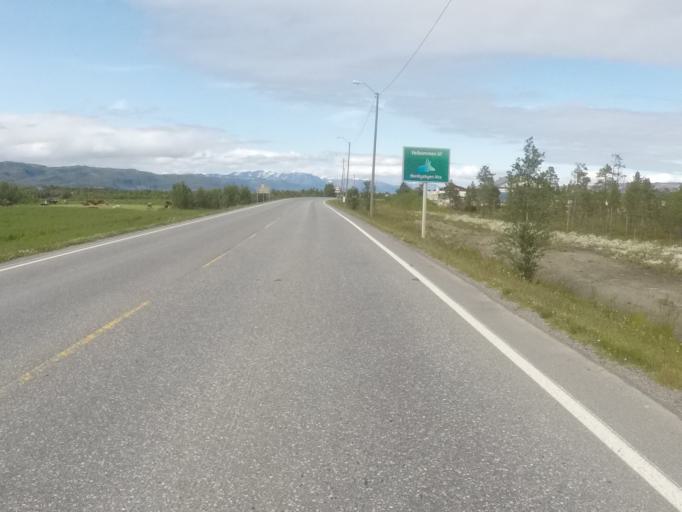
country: NO
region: Finnmark Fylke
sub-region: Alta
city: Alta
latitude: 69.9477
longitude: 23.2401
